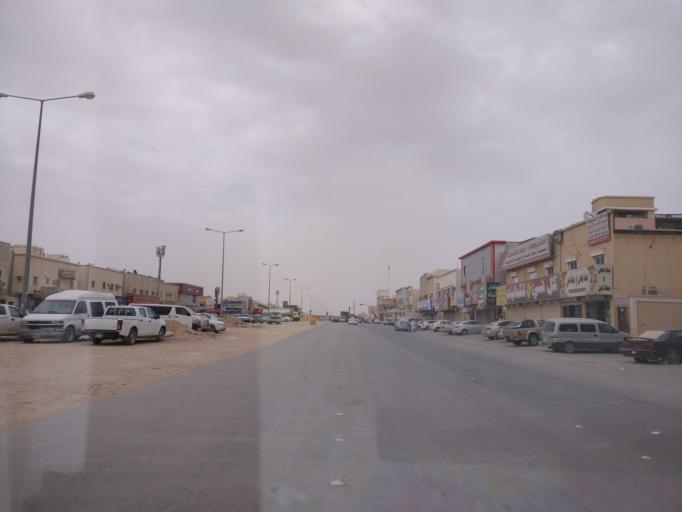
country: SA
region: Ar Riyad
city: Riyadh
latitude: 24.5757
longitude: 46.5762
